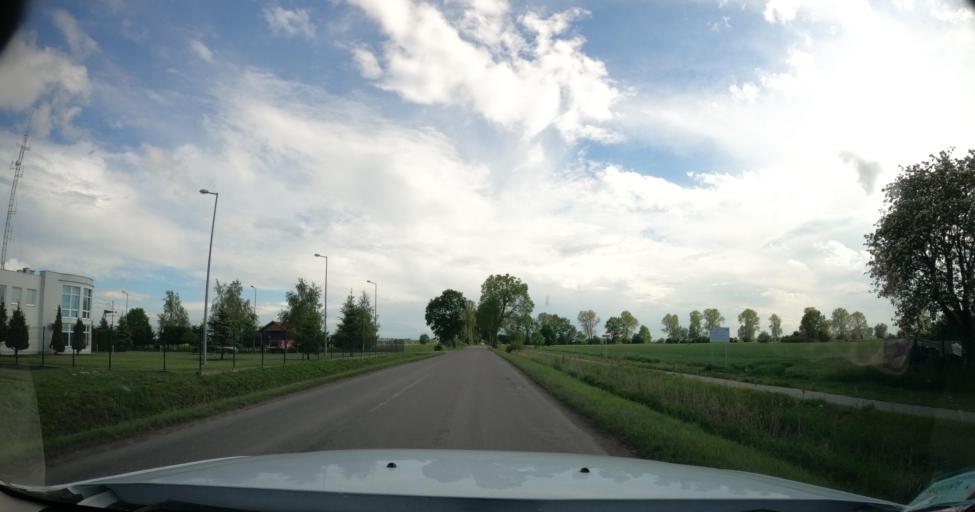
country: PL
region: Pomeranian Voivodeship
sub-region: Powiat nowodworski
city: Nowy Dwor Gdanski
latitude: 54.2059
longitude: 19.1369
